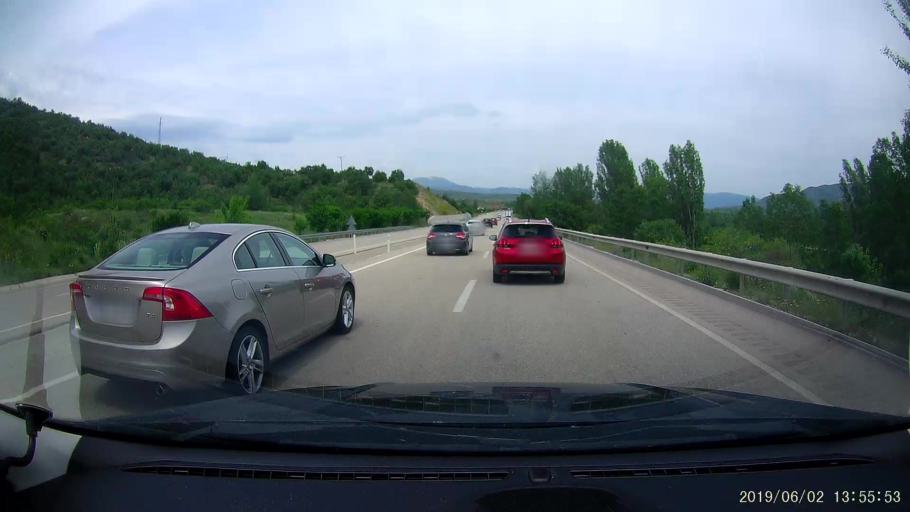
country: TR
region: Cankiri
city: Beloren
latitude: 40.8618
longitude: 33.4799
